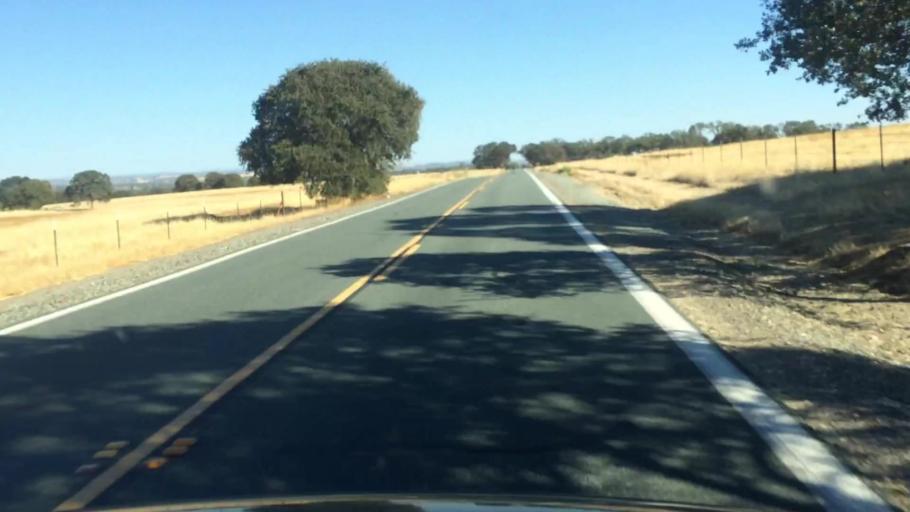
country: US
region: California
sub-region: Amador County
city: Ione
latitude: 38.3857
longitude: -121.0056
